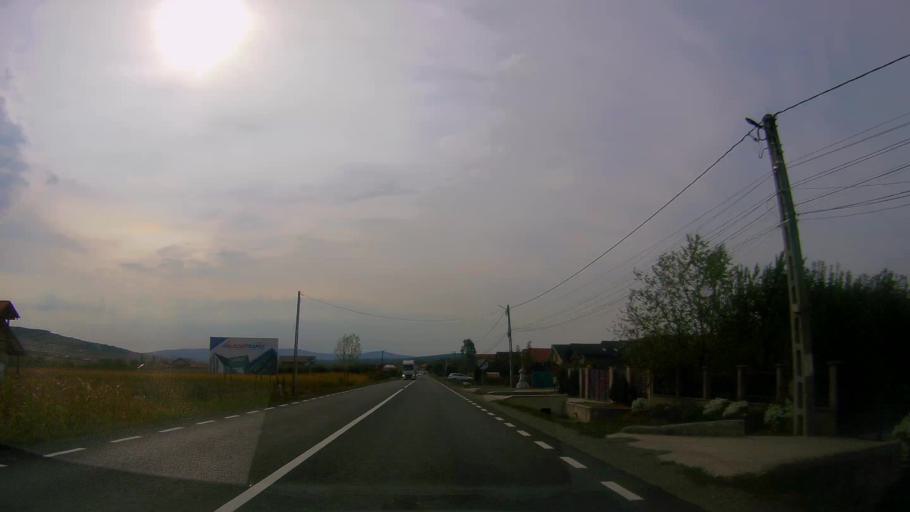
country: RO
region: Salaj
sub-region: Comuna Hereclean
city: Hereclean
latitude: 47.2501
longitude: 22.9839
